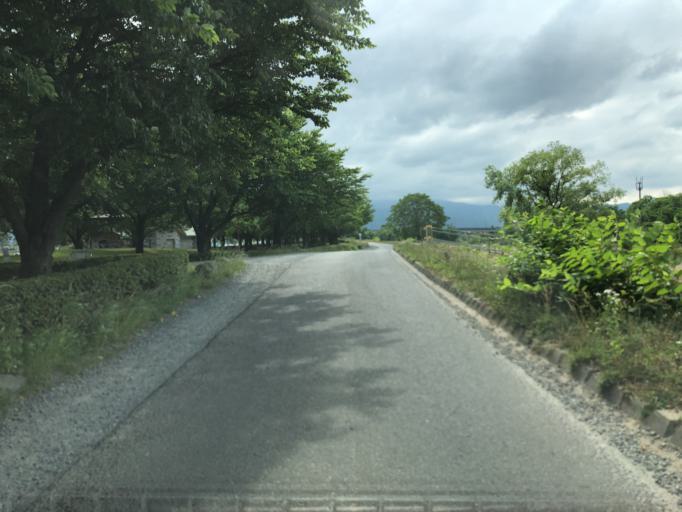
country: JP
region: Fukushima
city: Fukushima-shi
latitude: 37.7543
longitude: 140.4410
